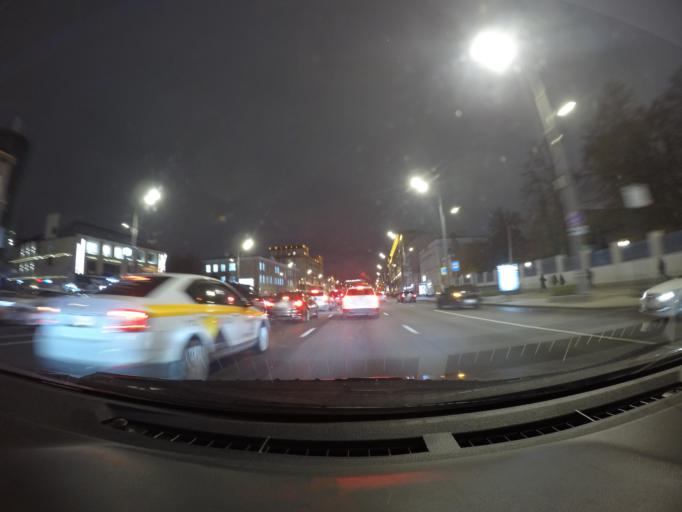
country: RU
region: Moskovskaya
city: Dorogomilovo
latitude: 55.7595
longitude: 37.5851
